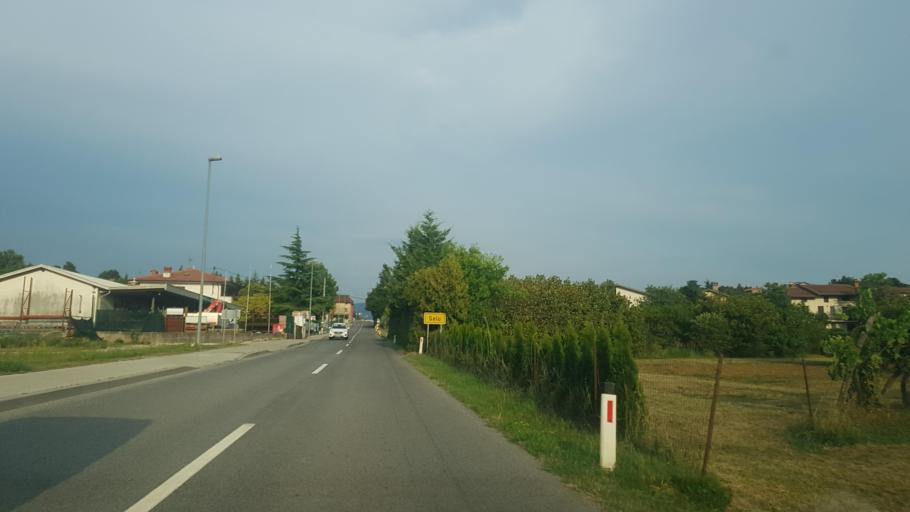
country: SI
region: Nova Gorica
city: Sempas
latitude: 45.8936
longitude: 13.7868
